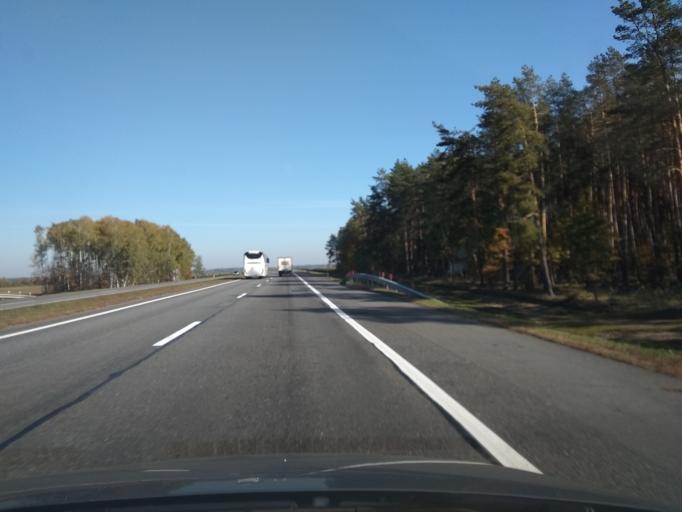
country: BY
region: Brest
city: Nyakhachava
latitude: 52.6584
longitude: 25.2729
